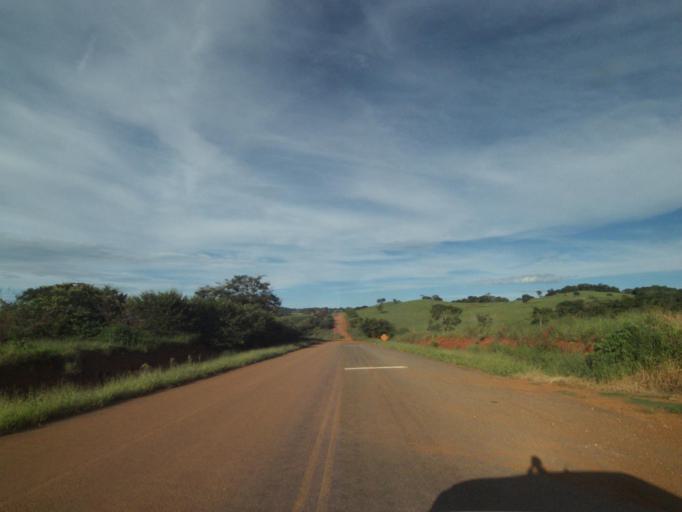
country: BR
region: Goias
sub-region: Jaragua
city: Jaragua
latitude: -15.8990
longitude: -49.5271
